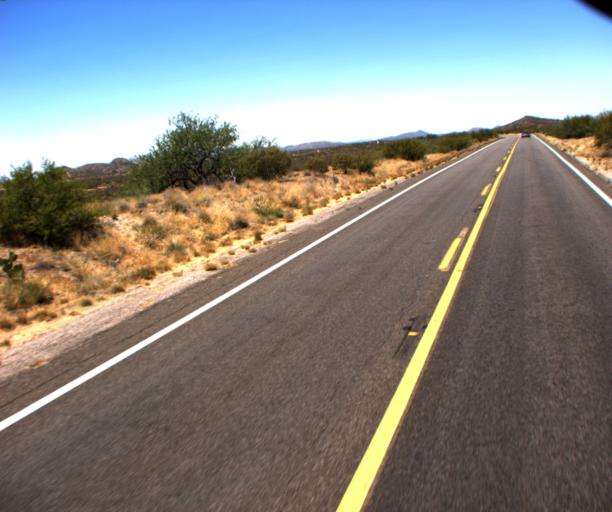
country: US
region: Arizona
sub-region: Pima County
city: Catalina
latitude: 32.6436
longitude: -111.0177
